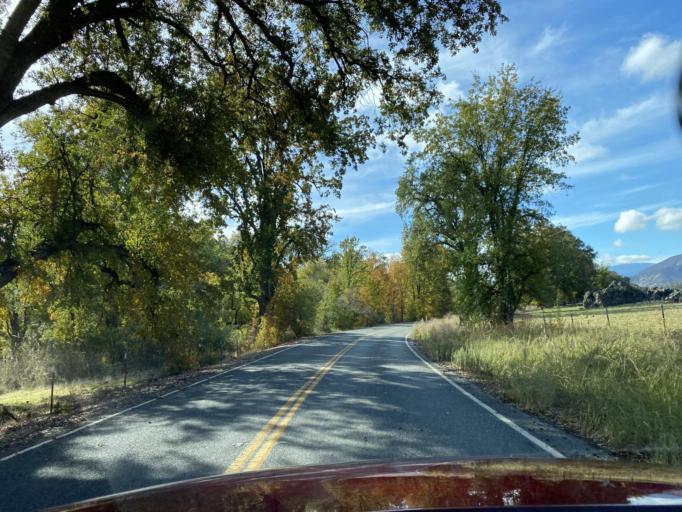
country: US
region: California
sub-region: Glenn County
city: Willows
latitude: 39.4181
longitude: -122.5375
